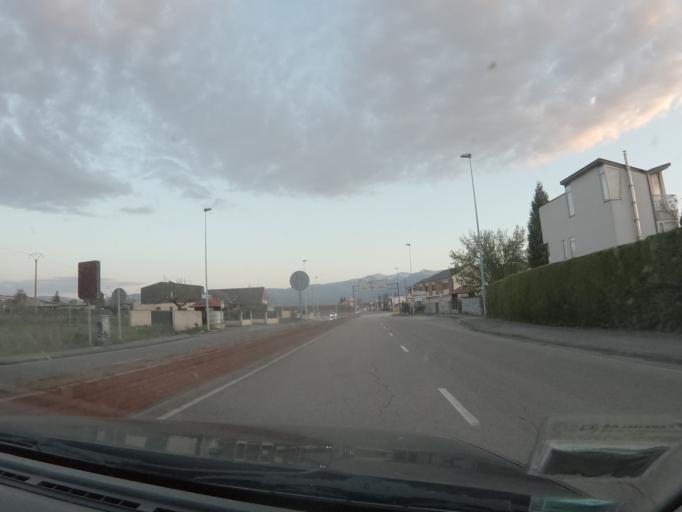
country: ES
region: Castille and Leon
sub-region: Provincia de Leon
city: Ponferrada
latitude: 42.5717
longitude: -6.6083
